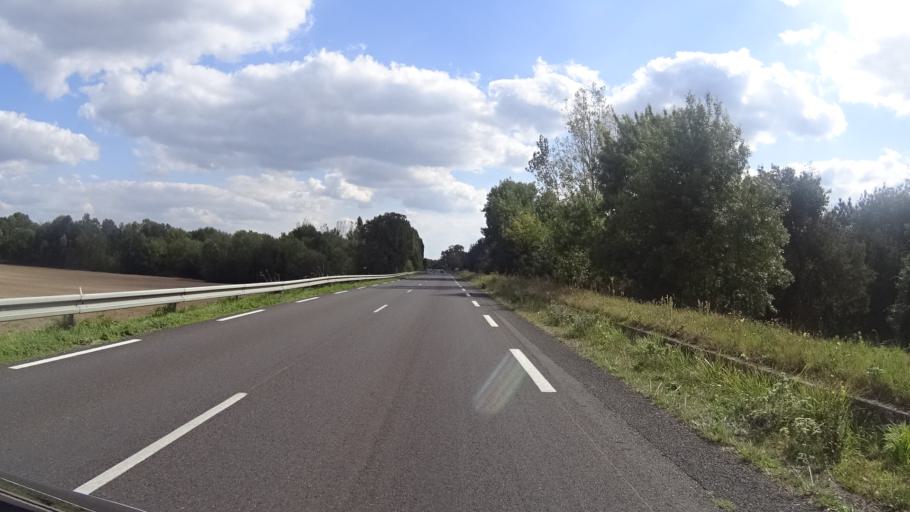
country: FR
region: Pays de la Loire
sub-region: Departement de Maine-et-Loire
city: Gennes
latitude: 47.3633
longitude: -0.2494
